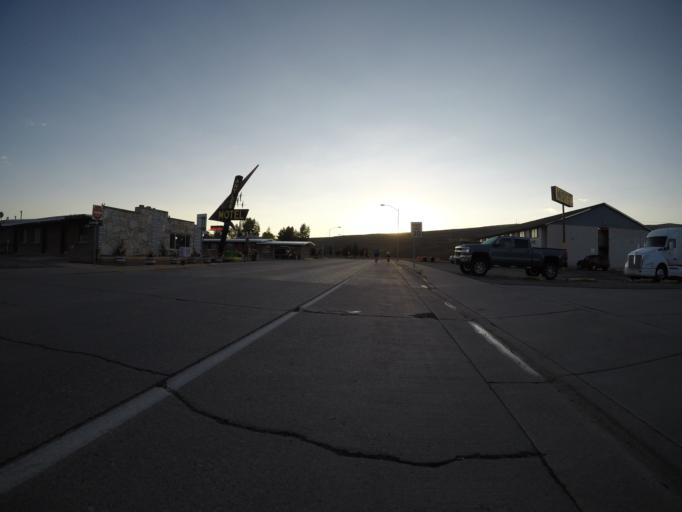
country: US
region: Wyoming
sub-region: Lincoln County
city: Kemmerer
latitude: 41.7895
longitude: -110.5378
